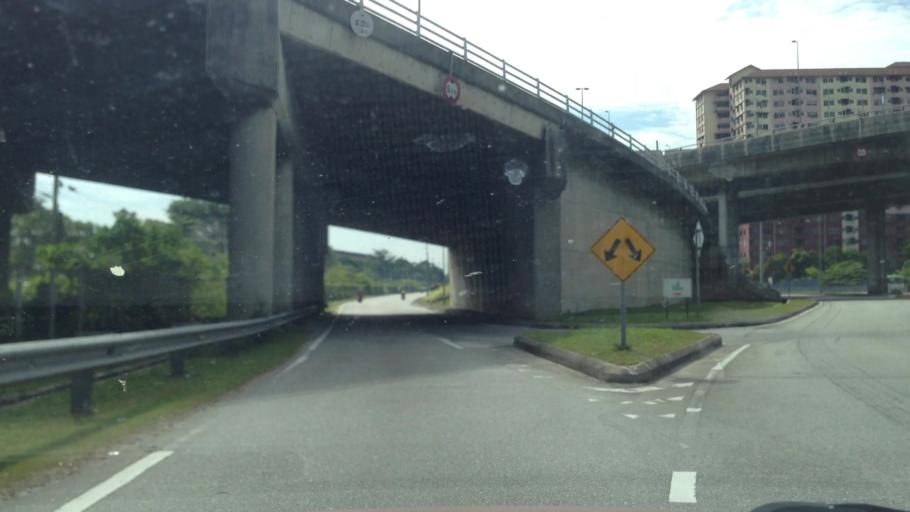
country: MY
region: Selangor
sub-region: Petaling
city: Petaling Jaya
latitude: 3.0847
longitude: 101.6254
